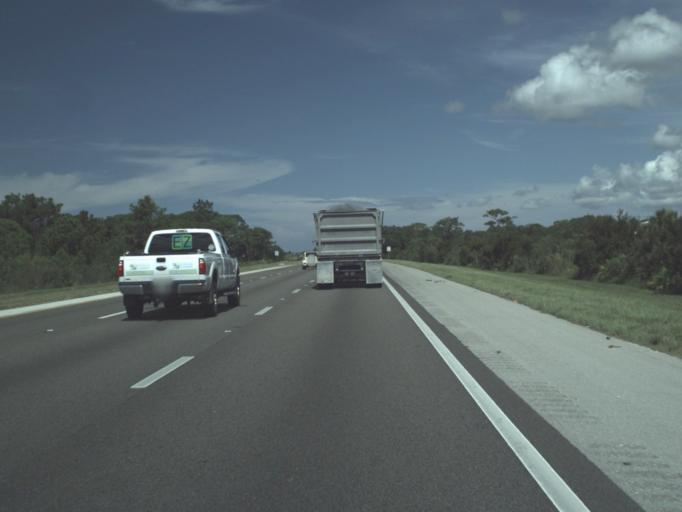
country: US
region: Florida
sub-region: Sarasota County
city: Nokomis
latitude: 27.1442
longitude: -82.4125
